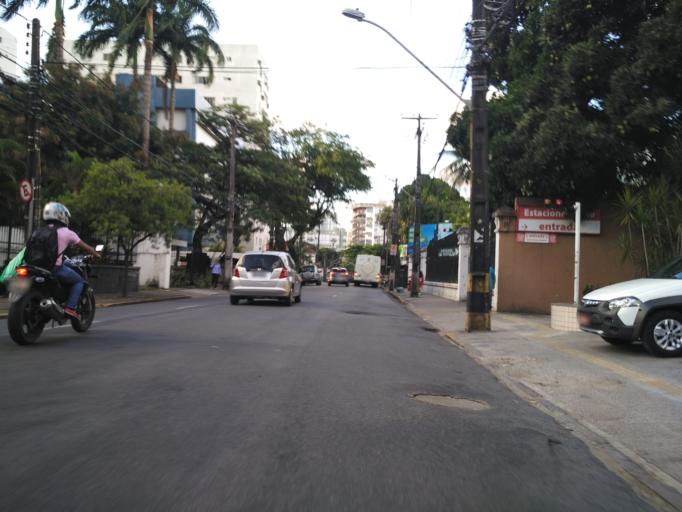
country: BR
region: Pernambuco
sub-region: Recife
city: Recife
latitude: -8.0433
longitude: -34.8974
